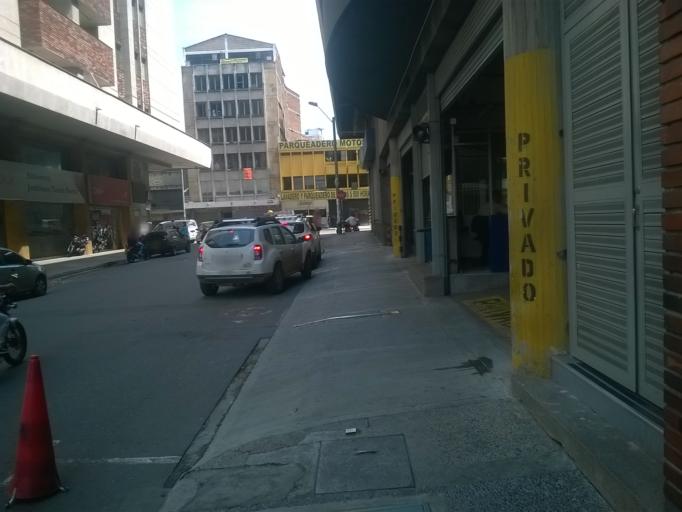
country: CO
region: Antioquia
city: Medellin
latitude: 6.2514
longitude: -75.5730
